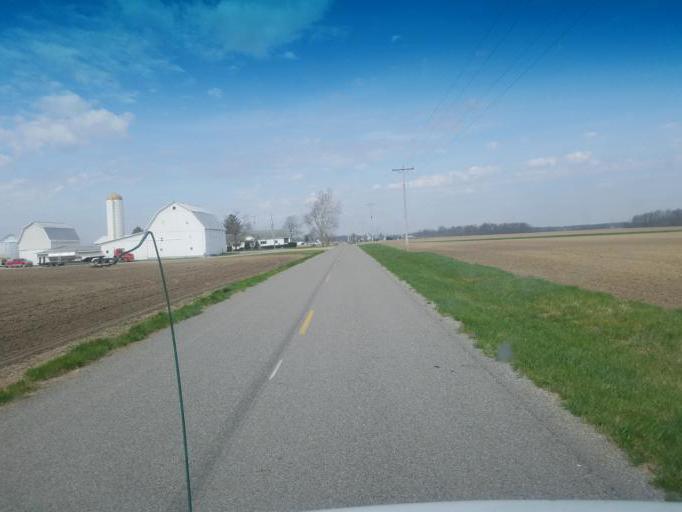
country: US
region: Ohio
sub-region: Logan County
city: Northwood
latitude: 40.4957
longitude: -83.5949
